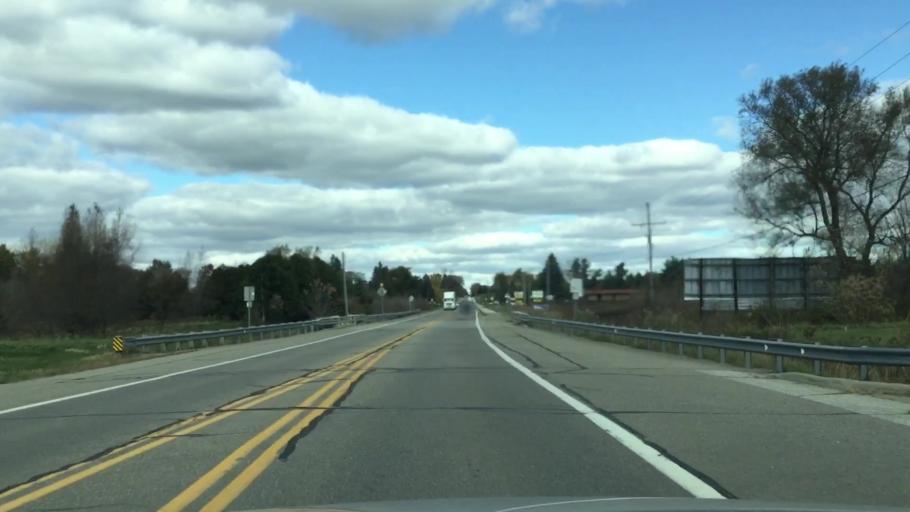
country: US
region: Michigan
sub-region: Lapeer County
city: Lapeer
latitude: 43.0911
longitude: -83.3077
